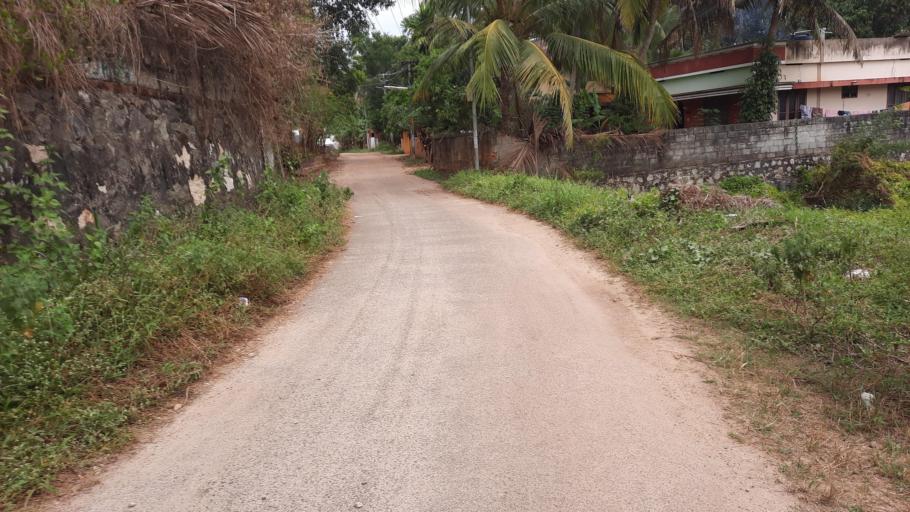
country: IN
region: Kerala
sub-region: Thiruvananthapuram
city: Thiruvananthapuram
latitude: 8.5589
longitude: 76.9318
